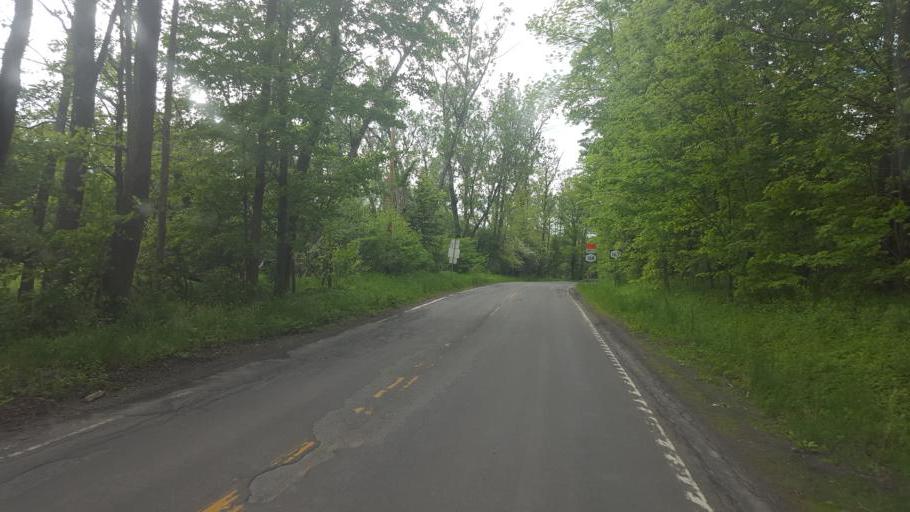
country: US
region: New York
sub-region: Otsego County
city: Richfield Springs
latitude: 42.8826
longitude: -74.9627
